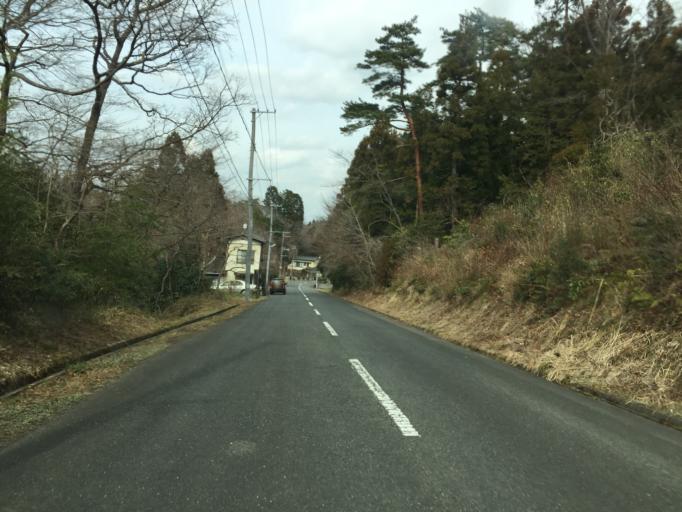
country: JP
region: Ibaraki
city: Kitaibaraki
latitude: 36.8729
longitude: 140.7831
